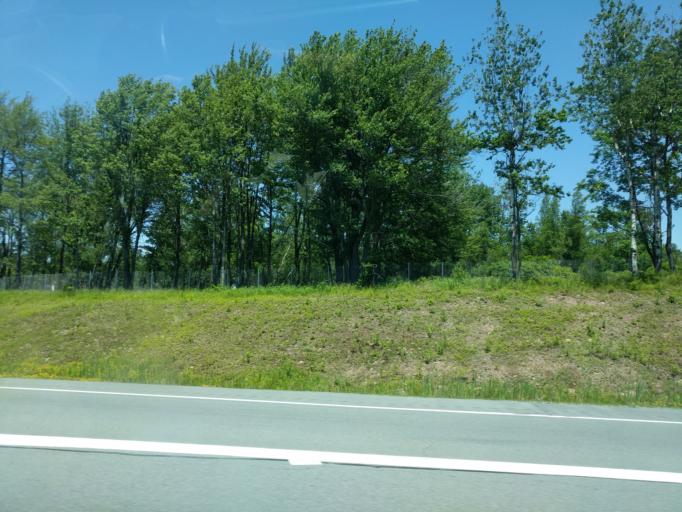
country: US
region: New York
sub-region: Sullivan County
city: Monticello
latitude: 41.6423
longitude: -74.6447
